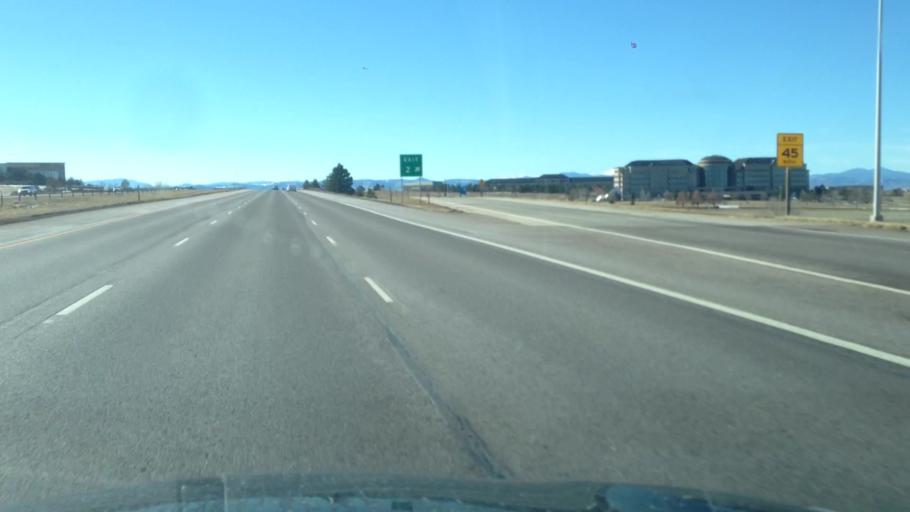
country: US
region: Colorado
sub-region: Douglas County
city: Meridian
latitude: 39.5537
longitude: -104.8346
